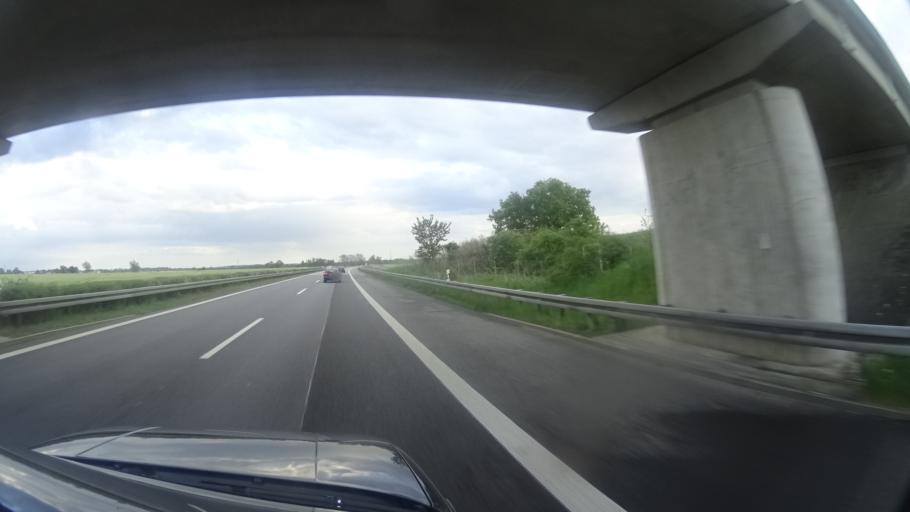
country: DE
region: Brandenburg
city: Wittstock
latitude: 53.1920
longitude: 12.4570
